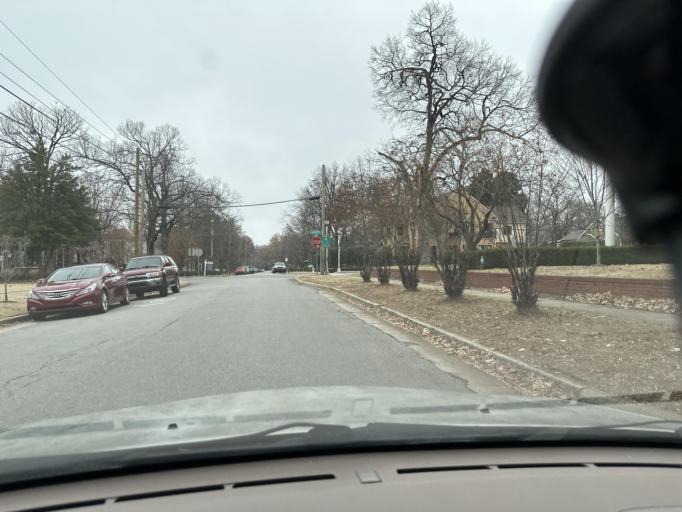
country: US
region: Arkansas
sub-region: Washington County
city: Fayetteville
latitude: 36.0681
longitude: -94.1561
